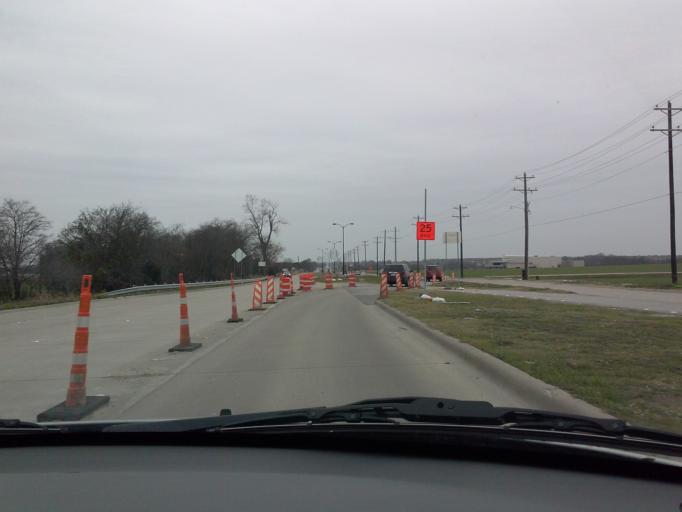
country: US
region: Texas
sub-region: Collin County
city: Frisco
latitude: 33.1517
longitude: -96.7502
